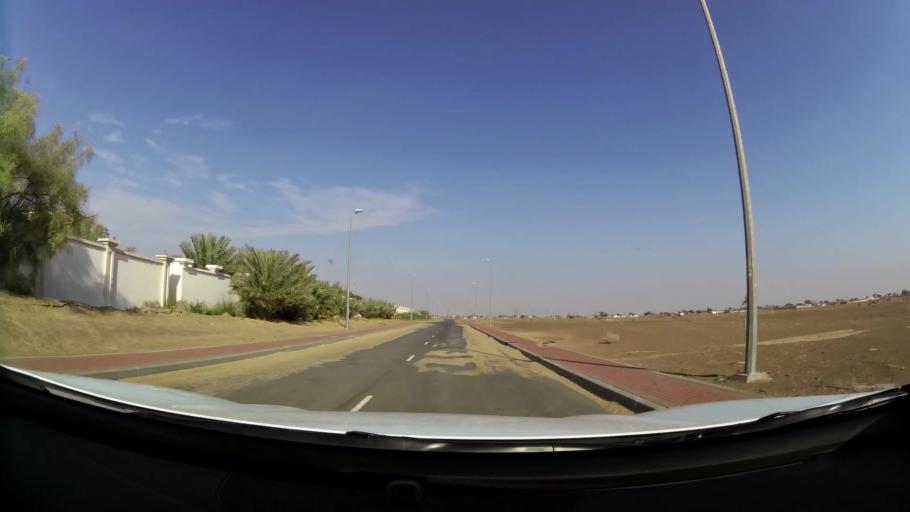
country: AE
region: Abu Dhabi
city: Al Ain
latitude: 24.0340
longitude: 55.8524
